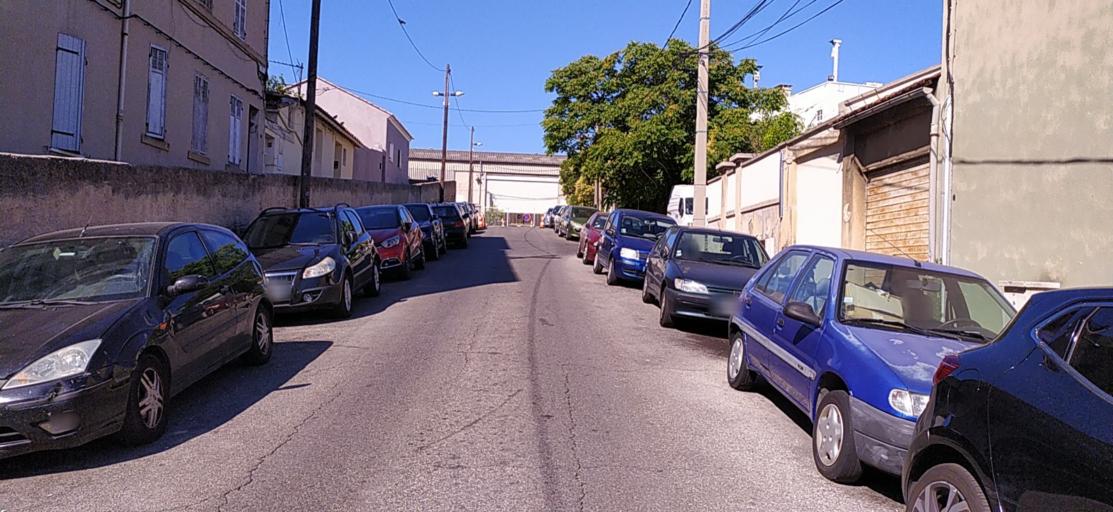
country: FR
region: Provence-Alpes-Cote d'Azur
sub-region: Departement des Bouches-du-Rhone
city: Marseille 14
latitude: 43.3392
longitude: 5.3610
